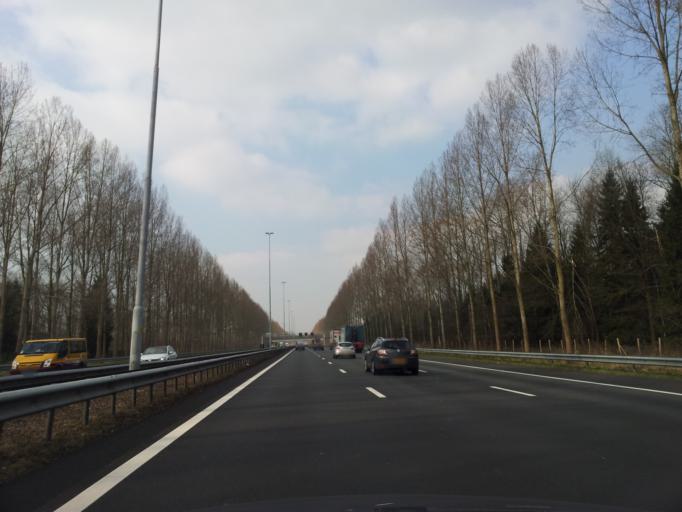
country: NL
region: North Brabant
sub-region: Gemeente Best
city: Best
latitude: 51.5349
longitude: 5.3816
